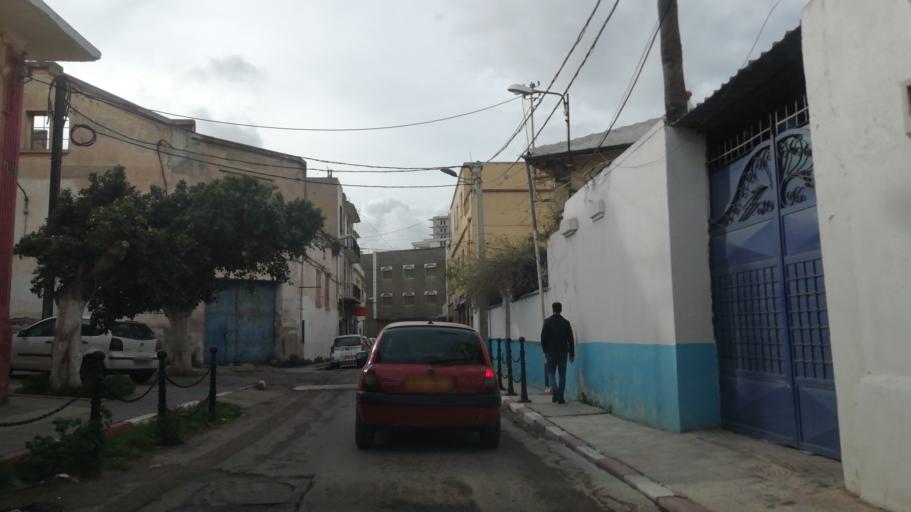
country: DZ
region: Oran
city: Oran
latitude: 35.6998
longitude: -0.6250
